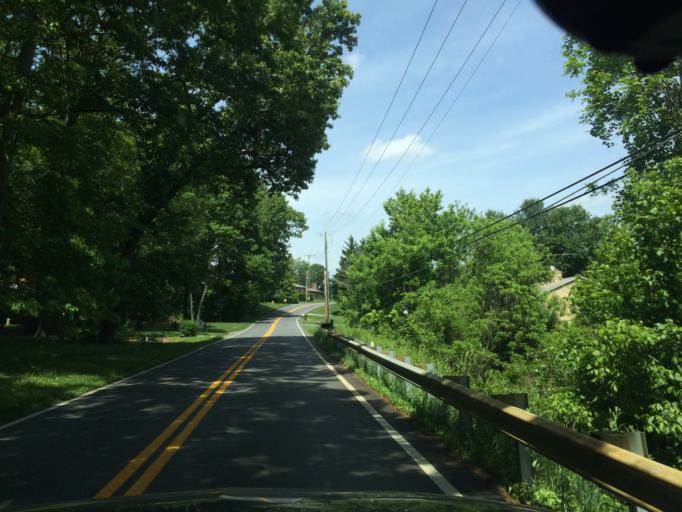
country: US
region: Maryland
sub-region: Carroll County
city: Westminster
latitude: 39.5294
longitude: -76.9414
